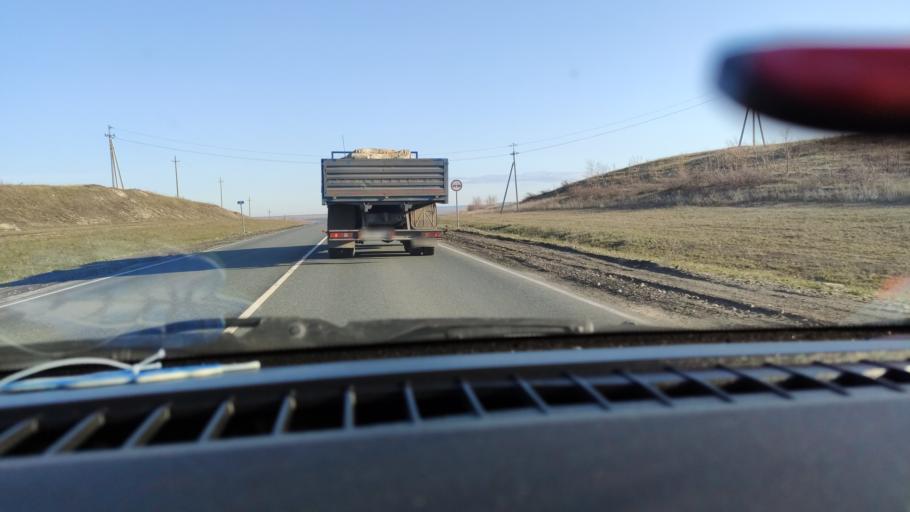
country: RU
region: Saratov
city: Alekseyevka
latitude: 52.3223
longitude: 47.9216
